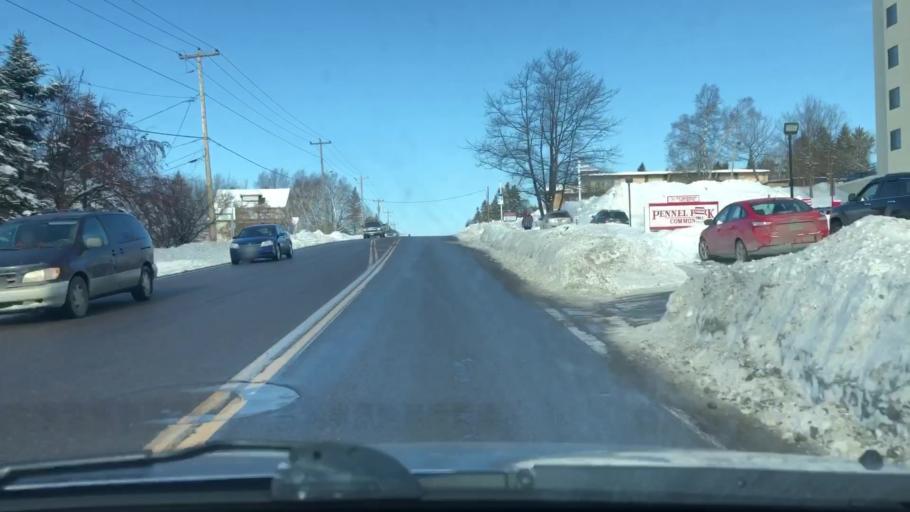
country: US
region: Minnesota
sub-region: Saint Louis County
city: Duluth
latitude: 46.8013
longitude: -92.1322
